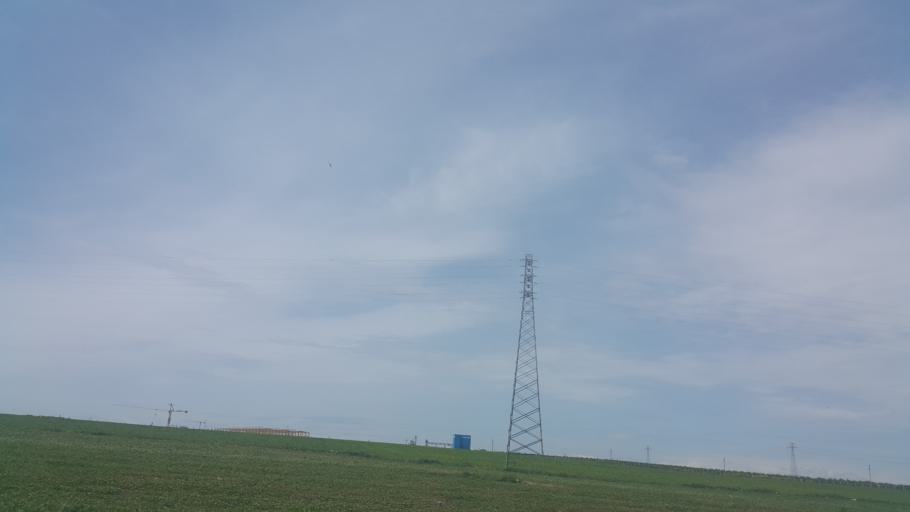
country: TR
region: Adana
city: Yakapinar
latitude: 36.9738
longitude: 35.6492
